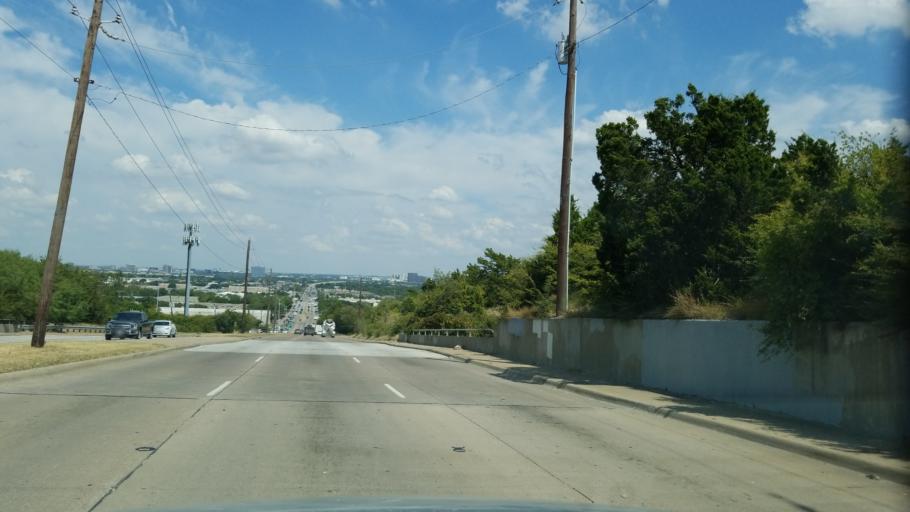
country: US
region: Texas
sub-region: Dallas County
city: Cockrell Hill
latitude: 32.7677
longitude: -96.8565
